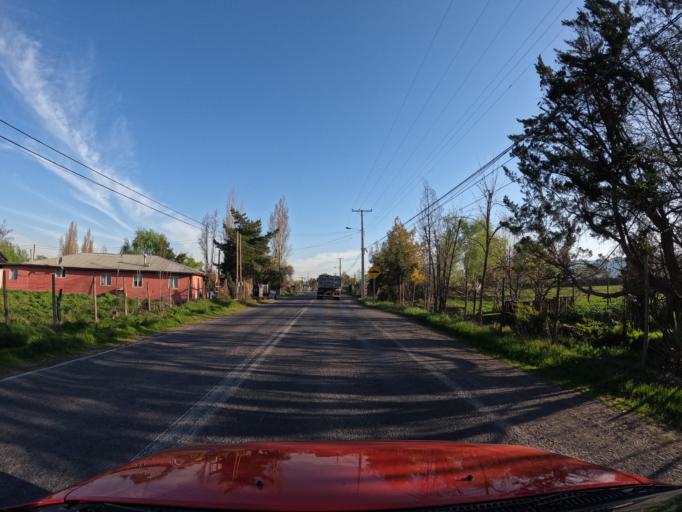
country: CL
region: Maule
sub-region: Provincia de Curico
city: Rauco
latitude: -34.8865
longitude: -71.2724
